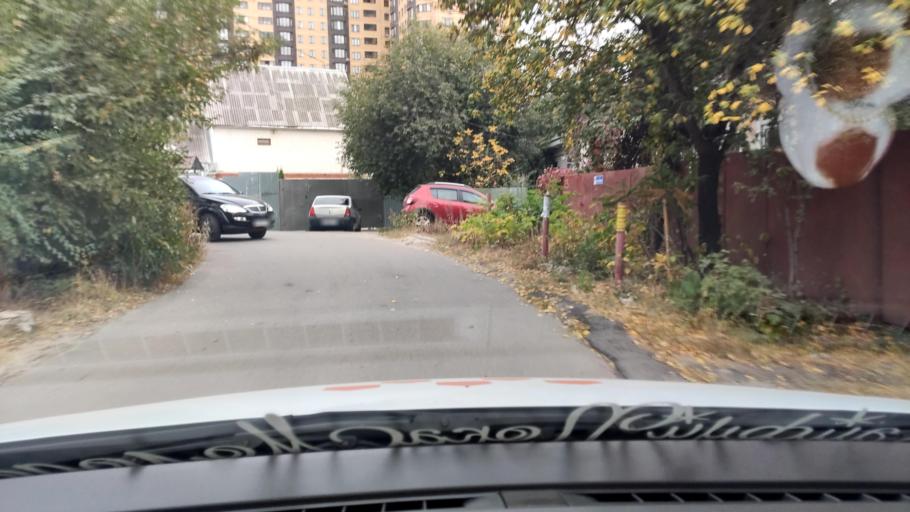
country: RU
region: Voronezj
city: Voronezh
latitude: 51.6743
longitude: 39.1632
